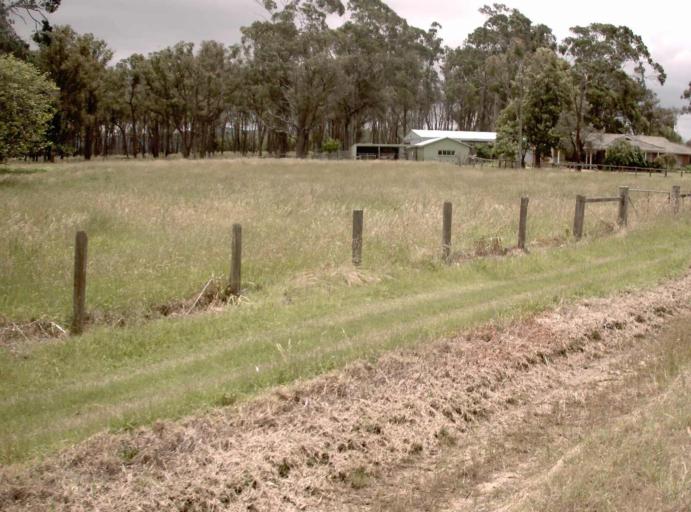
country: AU
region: Victoria
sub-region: Latrobe
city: Traralgon
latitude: -38.5416
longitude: 146.6565
